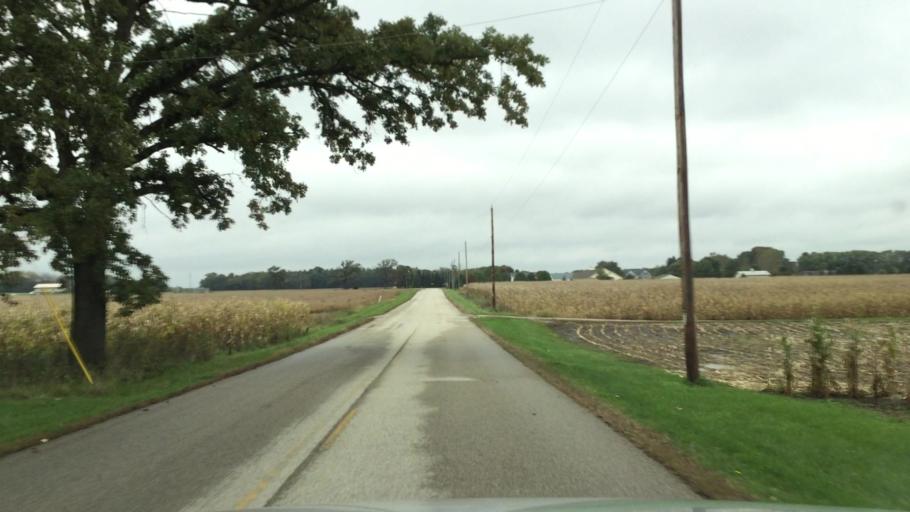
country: US
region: Wisconsin
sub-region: Racine County
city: Eagle Lake
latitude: 42.7519
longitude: -88.1554
